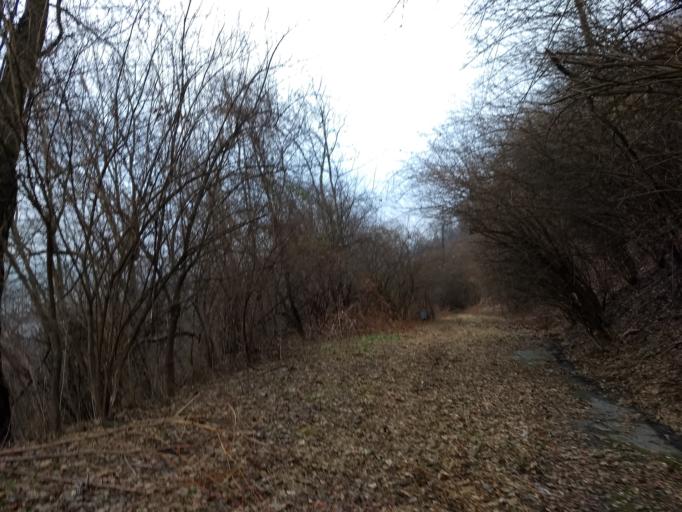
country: US
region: Pennsylvania
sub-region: Allegheny County
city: East Pittsburgh
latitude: 40.3875
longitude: -79.8467
